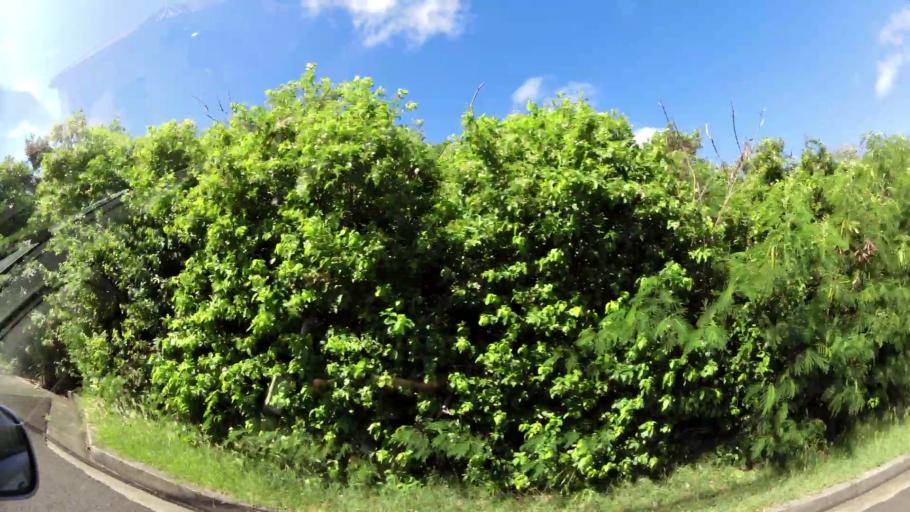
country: GD
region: Saint George
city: Saint George's
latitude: 11.9925
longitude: -61.7583
